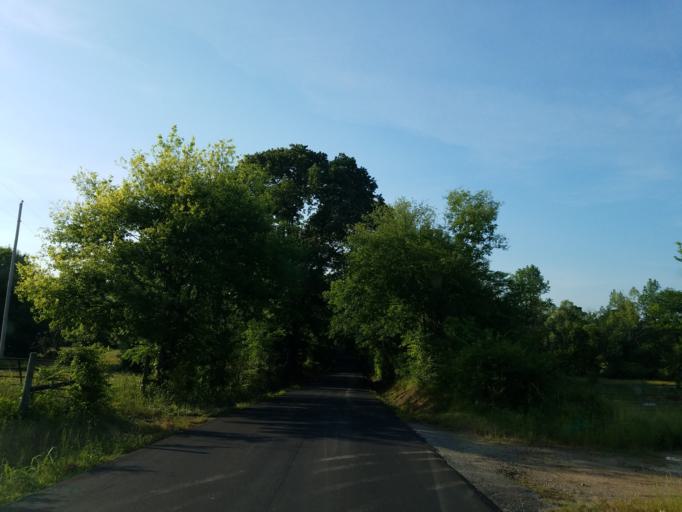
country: US
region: Georgia
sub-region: Gordon County
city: Calhoun
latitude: 34.5050
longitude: -85.1163
